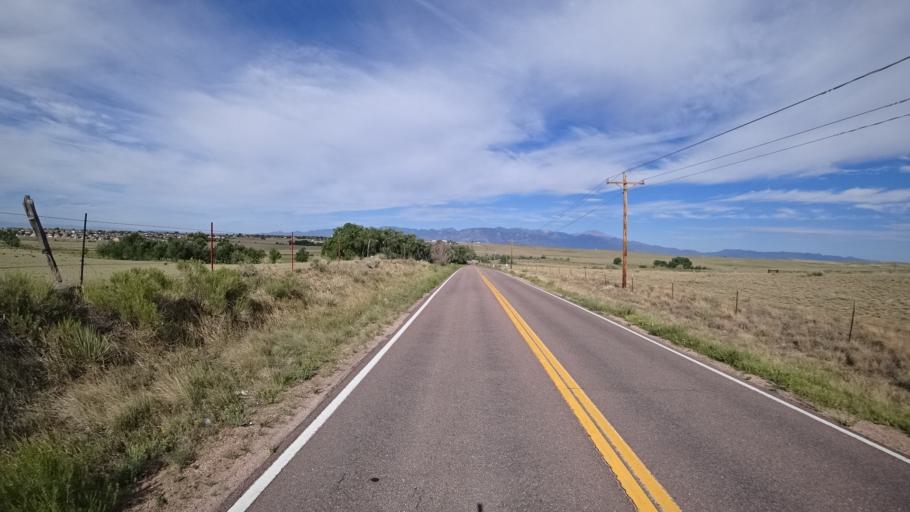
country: US
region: Colorado
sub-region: El Paso County
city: Security-Widefield
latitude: 38.7374
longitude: -104.6605
